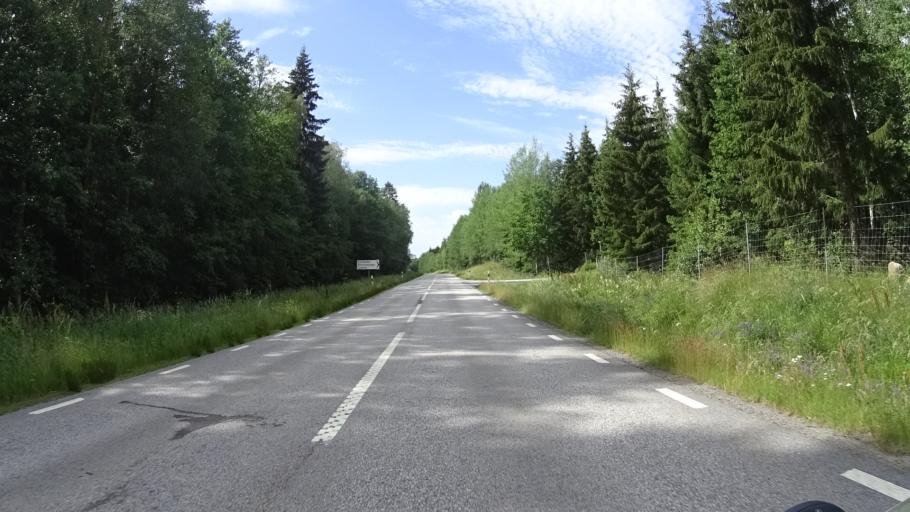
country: SE
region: OEstergoetland
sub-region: Atvidabergs Kommun
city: Atvidaberg
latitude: 58.1708
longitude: 16.0401
